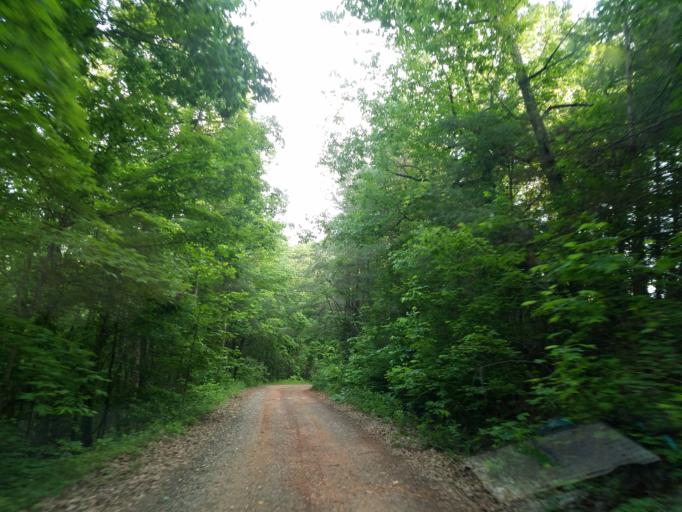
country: US
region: Georgia
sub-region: Dawson County
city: Dawsonville
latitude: 34.5753
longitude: -84.1430
